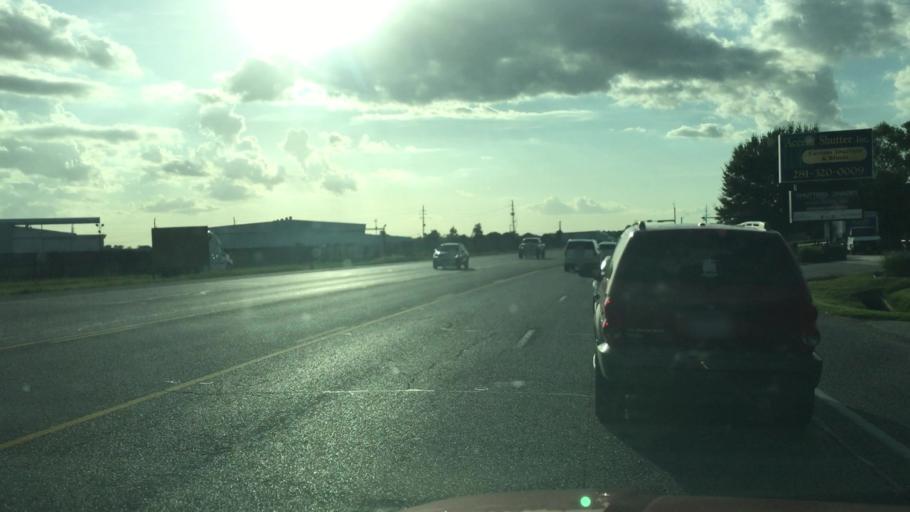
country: US
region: Texas
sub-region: Harris County
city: Tomball
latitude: 30.0739
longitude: -95.5539
